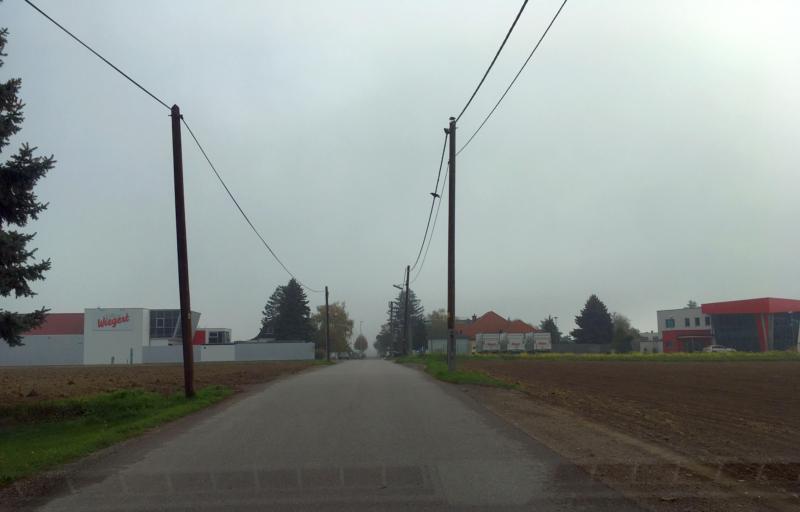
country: AT
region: Lower Austria
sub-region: Politischer Bezirk Ganserndorf
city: Gross-Enzersdorf
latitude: 48.2098
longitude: 16.4838
